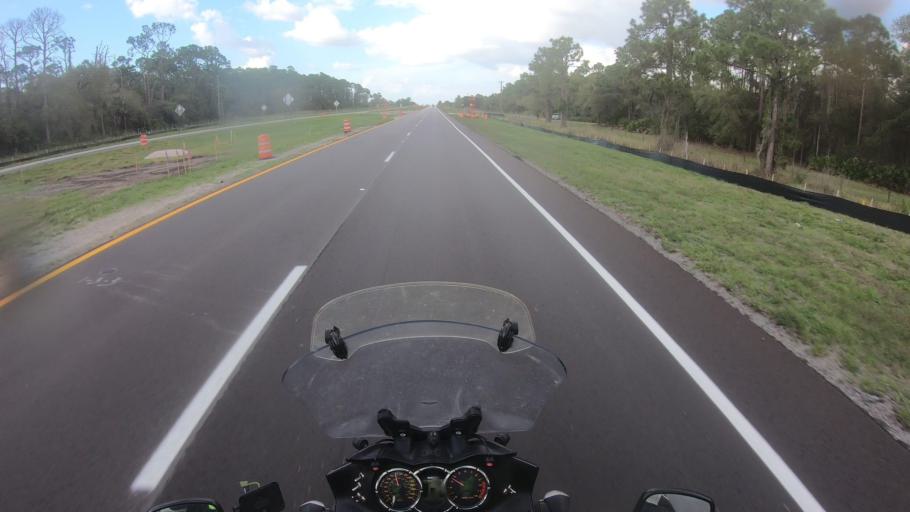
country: US
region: Florida
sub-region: Highlands County
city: Placid Lakes
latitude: 27.0565
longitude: -81.3360
